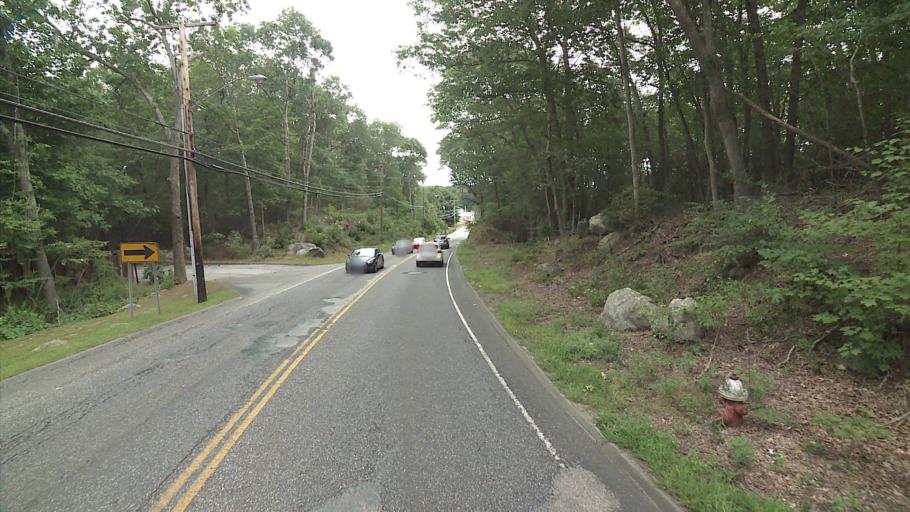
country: US
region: Connecticut
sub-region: New London County
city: Niantic
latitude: 41.3202
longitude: -72.2178
